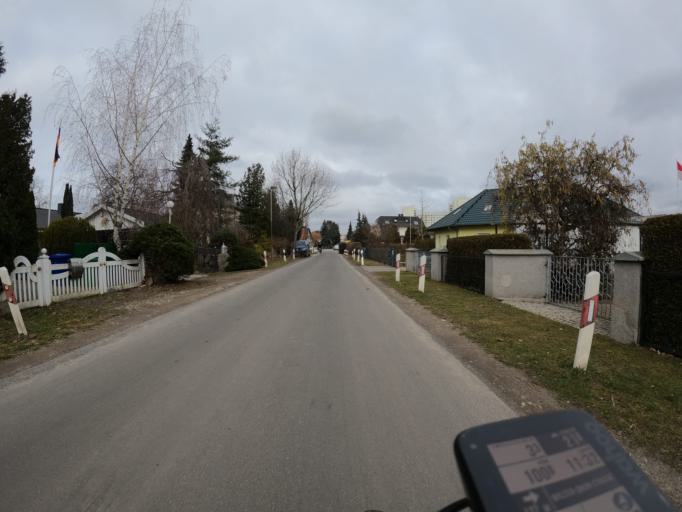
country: DE
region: Berlin
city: Buckow
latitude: 52.4151
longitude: 13.4444
